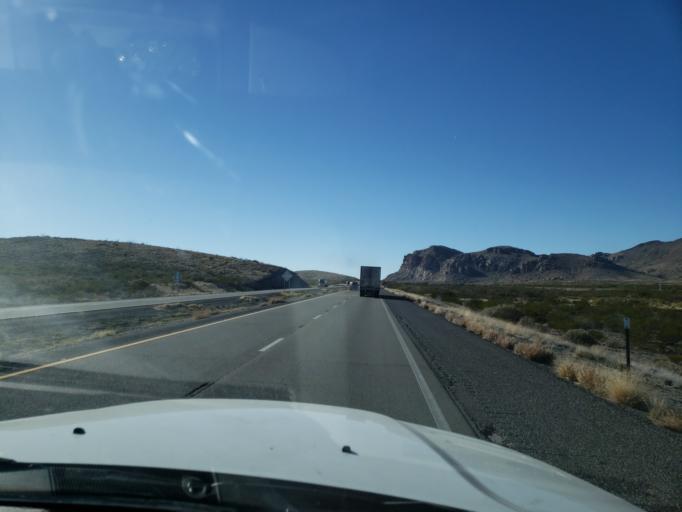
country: US
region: New Mexico
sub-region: Hidalgo County
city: Lordsburg
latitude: 32.2272
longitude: -108.9781
